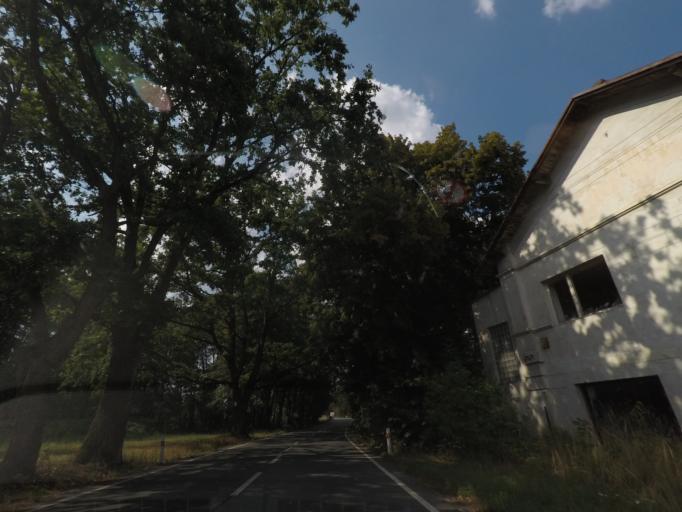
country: CZ
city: Albrechtice nad Orlici
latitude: 50.1283
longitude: 16.0645
